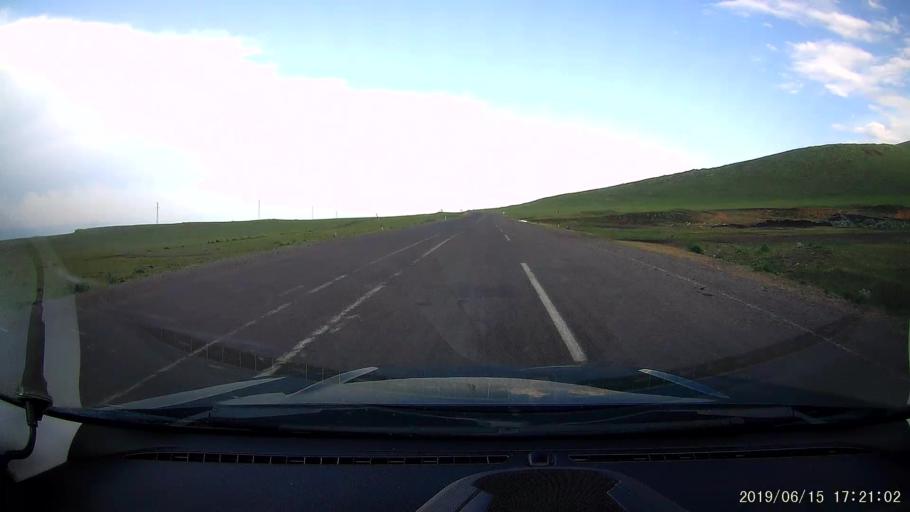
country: TR
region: Kars
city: Basgedikler
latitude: 40.6172
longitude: 43.3161
